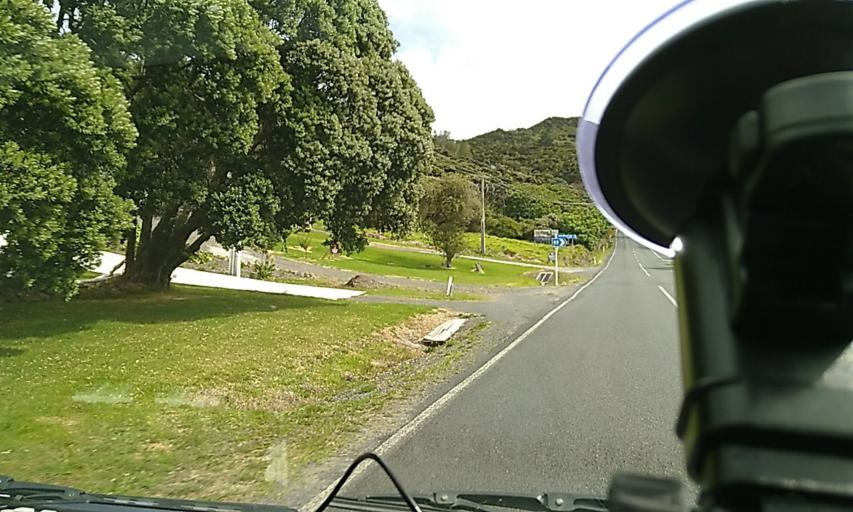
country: NZ
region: Northland
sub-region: Far North District
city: Ahipara
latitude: -35.5348
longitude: 173.3878
